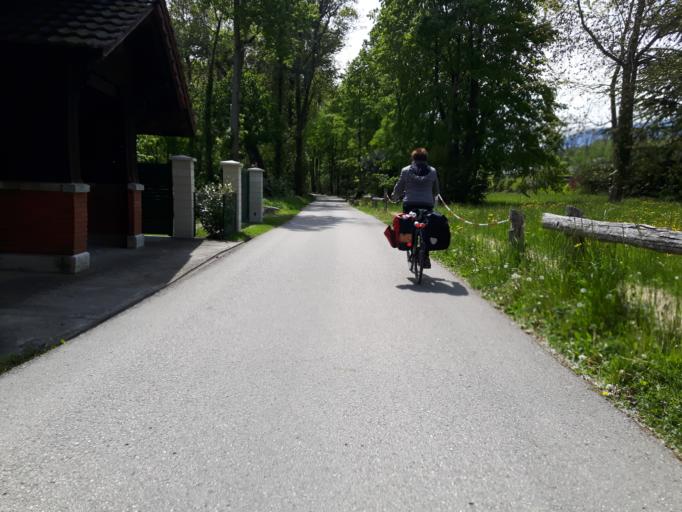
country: CH
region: Neuchatel
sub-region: Boudry District
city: Bevaix
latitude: 46.9225
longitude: 6.8181
